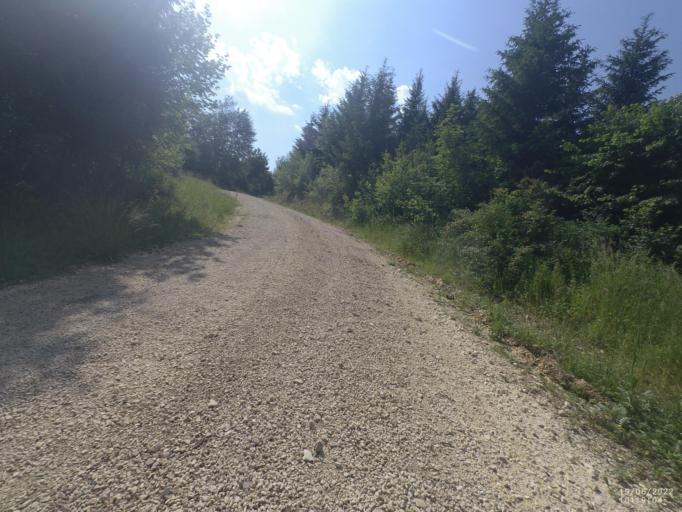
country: DE
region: Baden-Wuerttemberg
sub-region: Regierungsbezirk Stuttgart
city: Gerstetten
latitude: 48.6068
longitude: 9.9979
